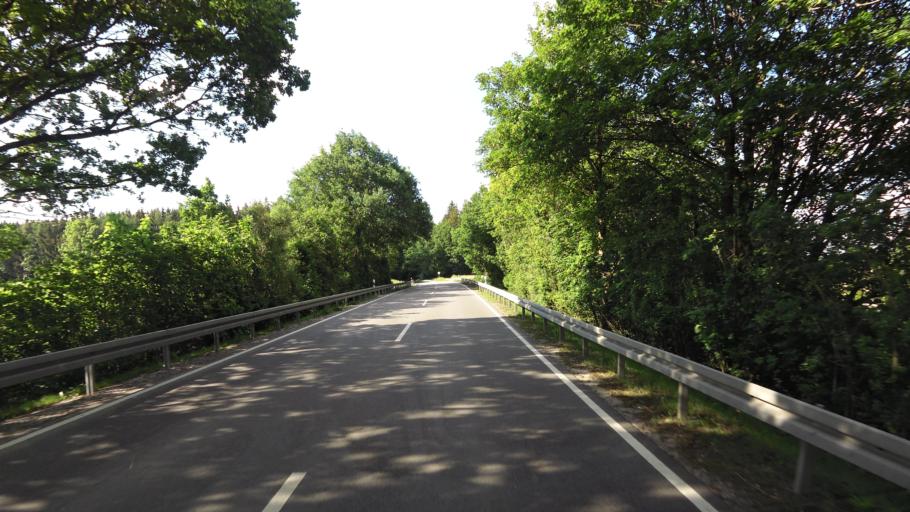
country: DE
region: Bavaria
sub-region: Upper Bavaria
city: Hohenpolding
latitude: 48.3984
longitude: 12.1302
